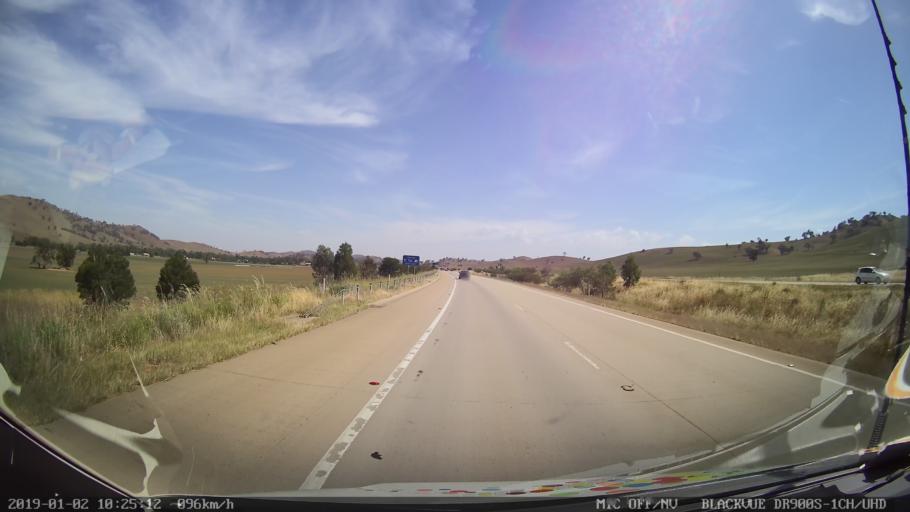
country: AU
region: New South Wales
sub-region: Gundagai
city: Gundagai
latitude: -34.9390
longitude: 148.1755
